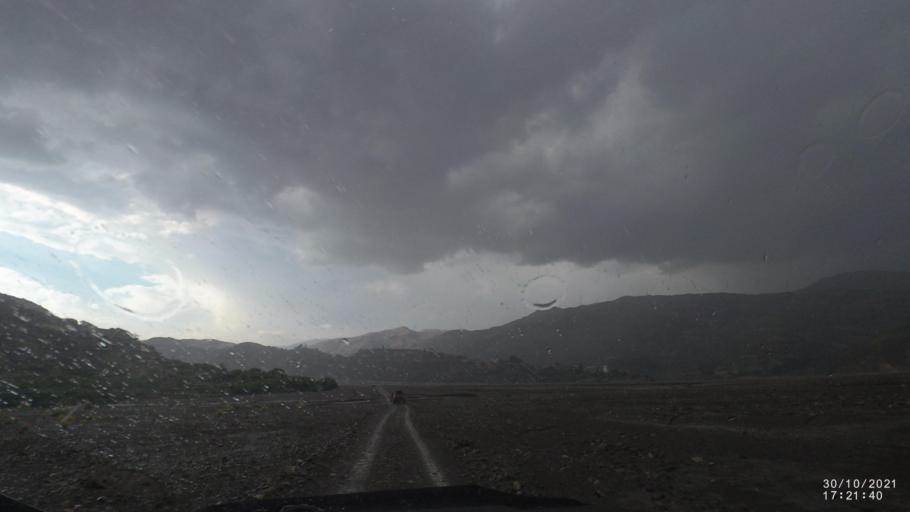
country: BO
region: Cochabamba
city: Colchani
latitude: -17.5251
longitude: -66.6210
